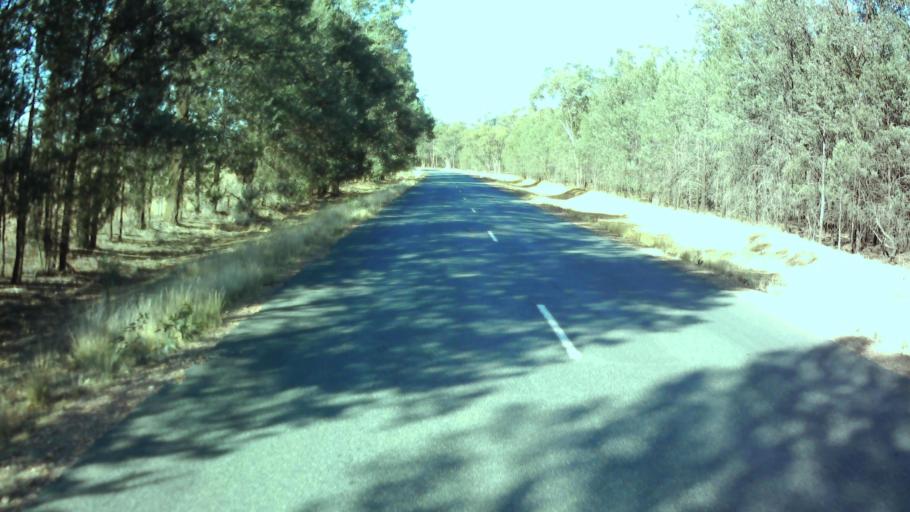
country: AU
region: New South Wales
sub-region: Weddin
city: Grenfell
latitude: -34.0207
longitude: 148.1023
